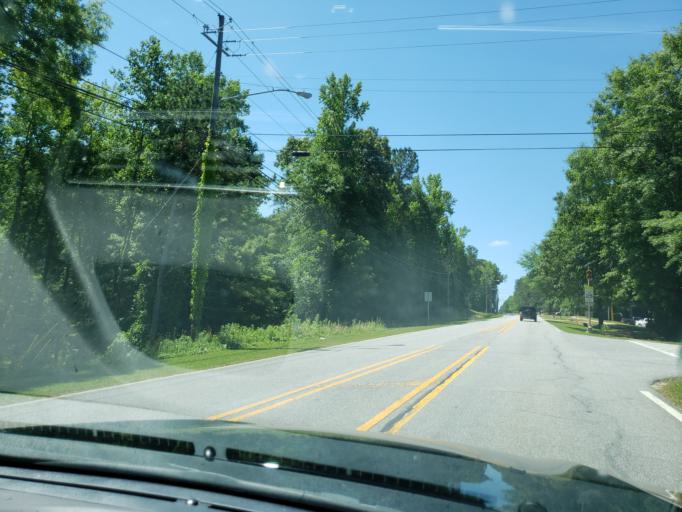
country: US
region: Alabama
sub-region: Lee County
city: Auburn
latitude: 32.6352
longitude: -85.4818
